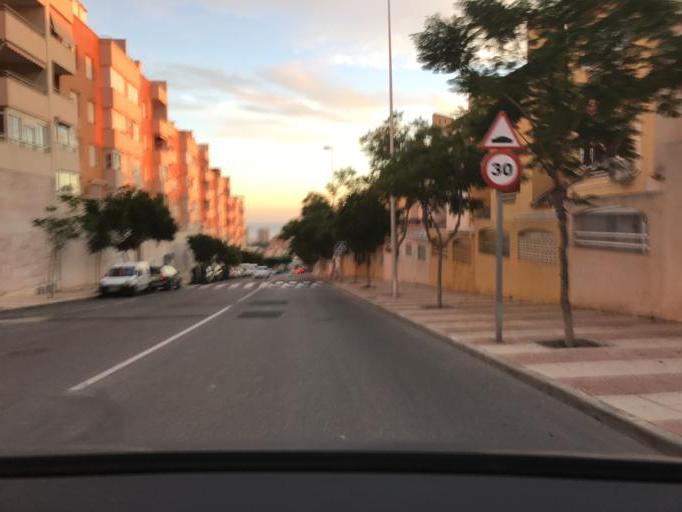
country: ES
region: Andalusia
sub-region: Provincia de Almeria
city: Aguadulce
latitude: 36.8197
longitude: -2.5824
